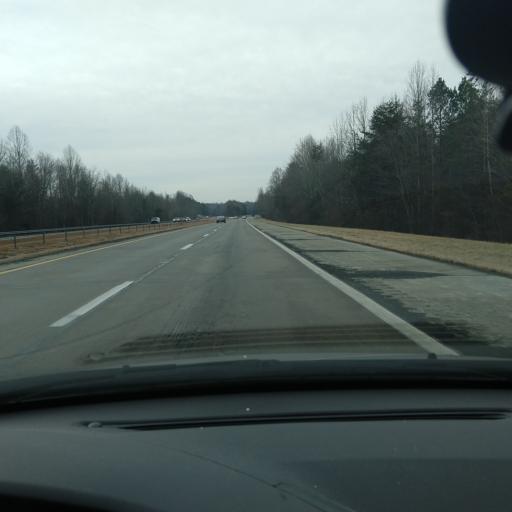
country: US
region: North Carolina
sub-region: Davidson County
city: Midway
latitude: 36.0035
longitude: -80.2370
